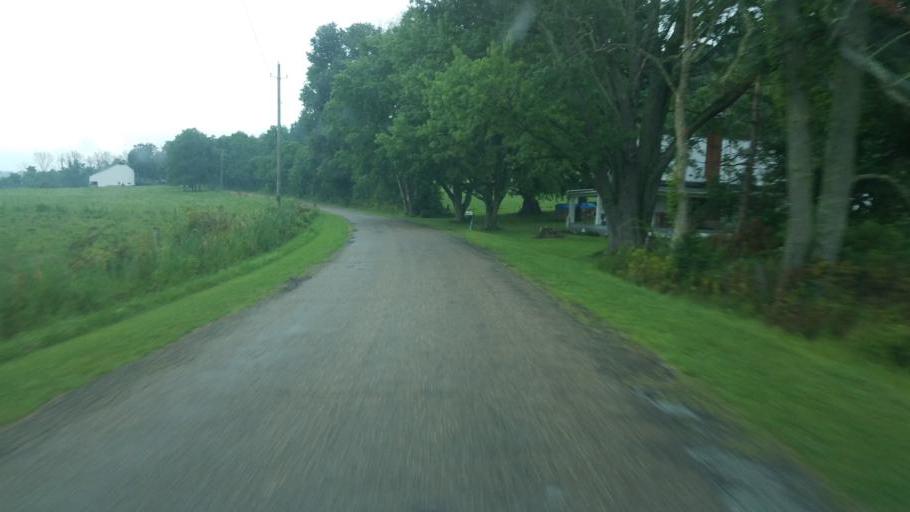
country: US
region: Ohio
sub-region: Tuscarawas County
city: Dennison
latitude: 40.3728
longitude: -81.2387
